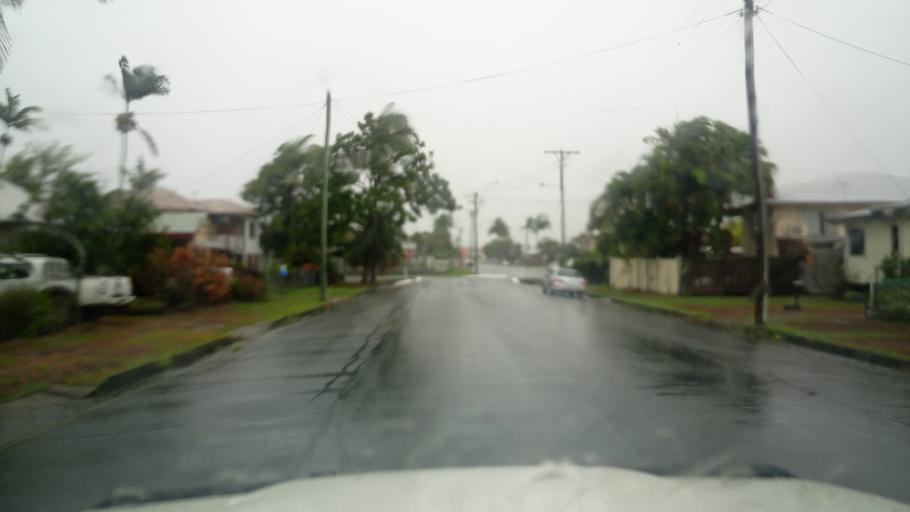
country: AU
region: Queensland
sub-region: Cairns
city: Cairns
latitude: -16.9373
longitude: 145.7618
